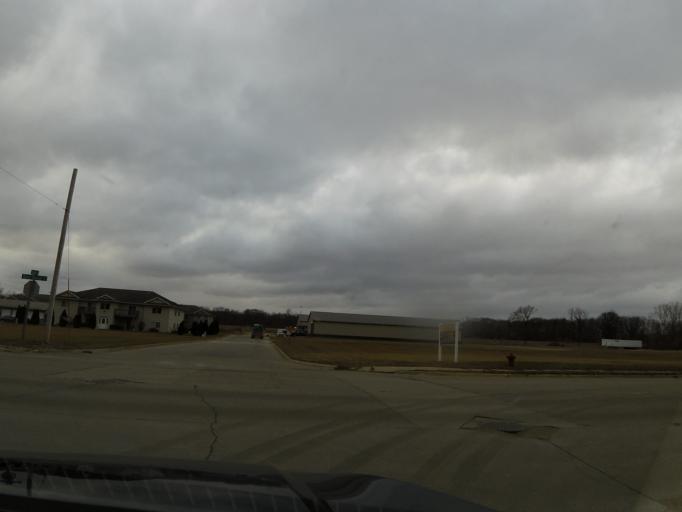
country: US
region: Iowa
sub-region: Black Hawk County
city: Evansdale
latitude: 42.4647
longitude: -92.2976
